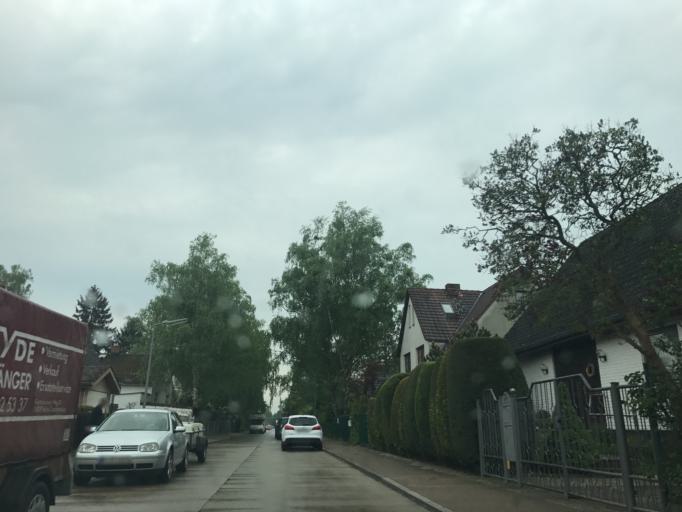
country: DE
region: Berlin
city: Staaken
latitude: 52.5502
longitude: 13.1511
